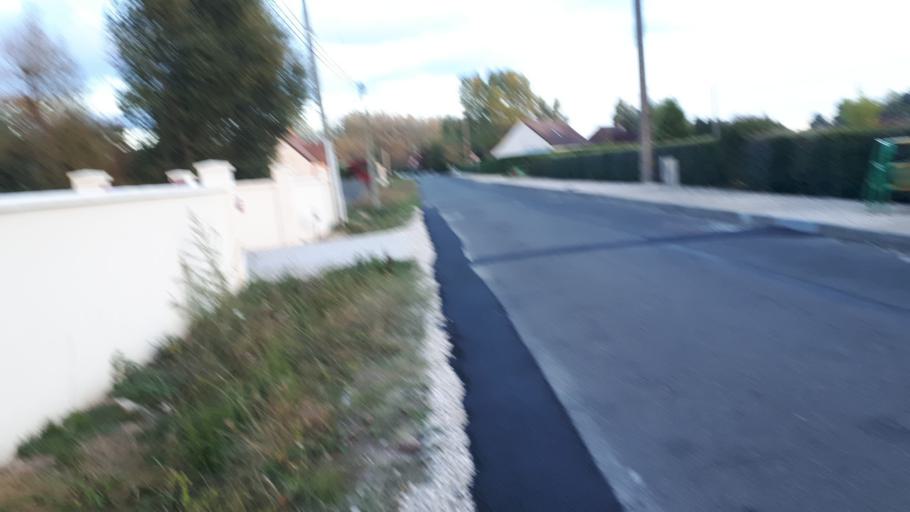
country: FR
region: Centre
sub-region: Departement du Loir-et-Cher
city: Saint-Romain-sur-Cher
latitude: 47.3625
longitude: 1.4049
